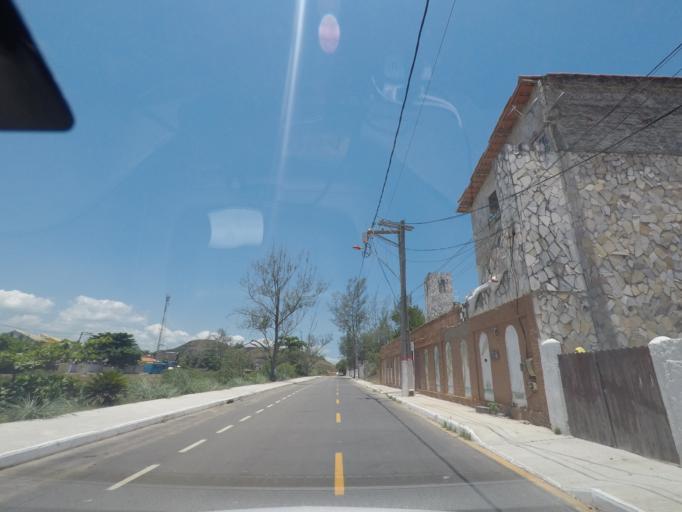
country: BR
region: Rio de Janeiro
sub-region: Niteroi
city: Niteroi
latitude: -22.9690
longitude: -43.0088
